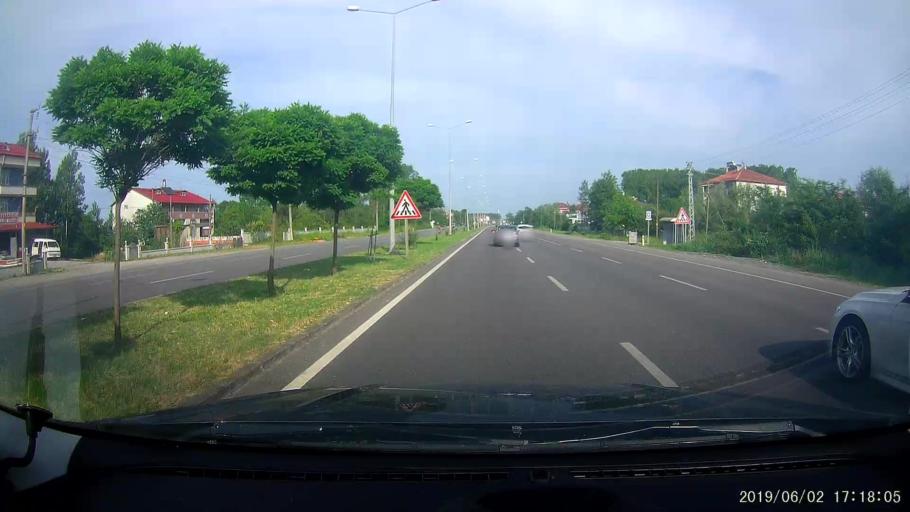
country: TR
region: Samsun
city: Dikbiyik
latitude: 41.2254
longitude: 36.5921
